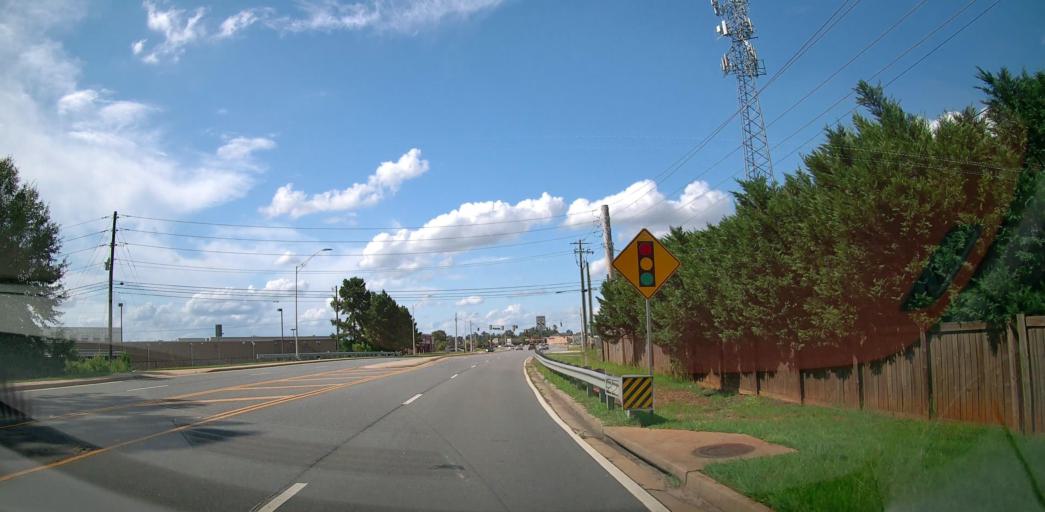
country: US
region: Georgia
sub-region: Houston County
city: Centerville
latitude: 32.5463
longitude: -83.6910
